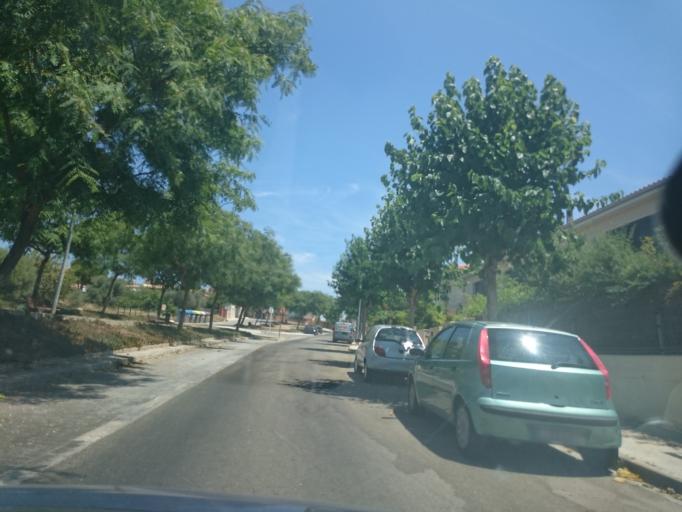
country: ES
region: Catalonia
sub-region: Provincia de Barcelona
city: Cubelles
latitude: 41.2179
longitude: 1.6799
